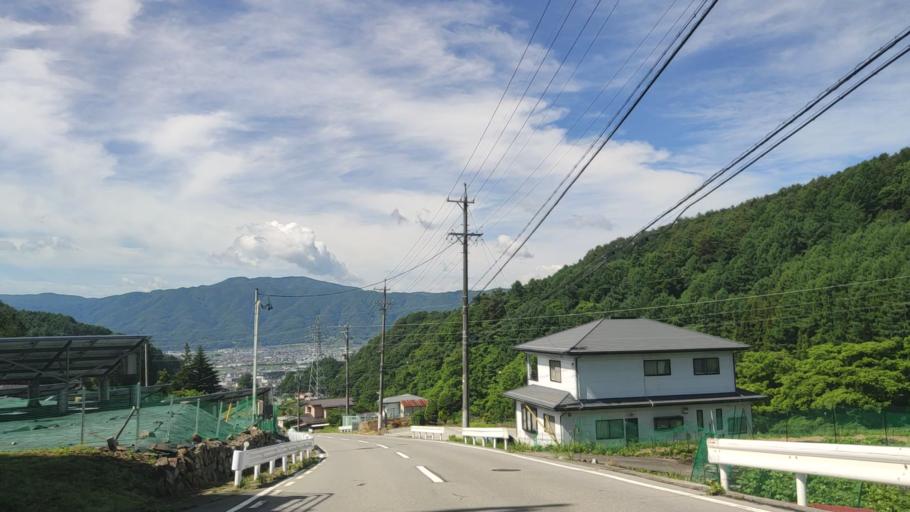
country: JP
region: Nagano
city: Suwa
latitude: 36.0582
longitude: 138.1303
